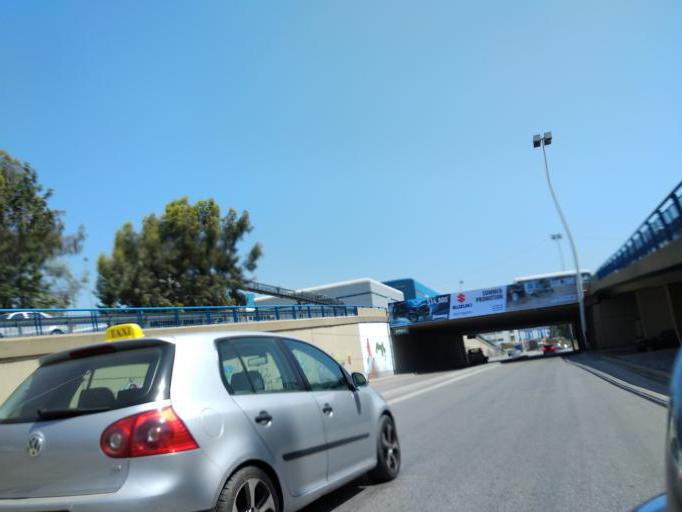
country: LB
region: Mont-Liban
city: Jdaidet el Matn
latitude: 33.8966
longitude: 35.5362
